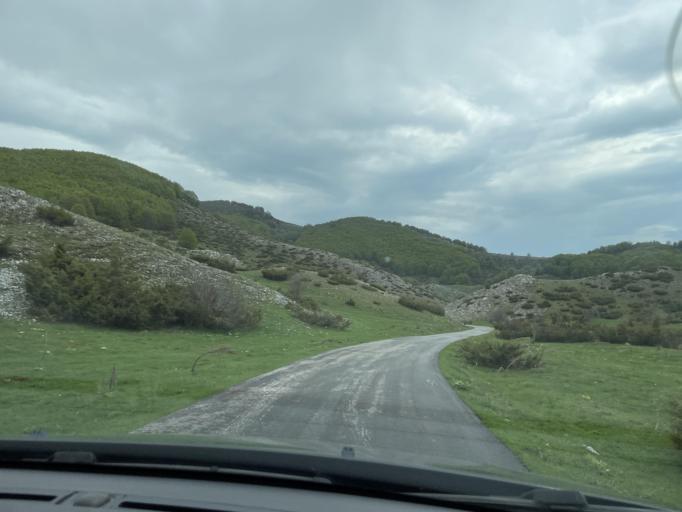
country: MK
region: Opstina Rostusa
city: Rostusha
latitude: 41.6057
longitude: 20.6850
